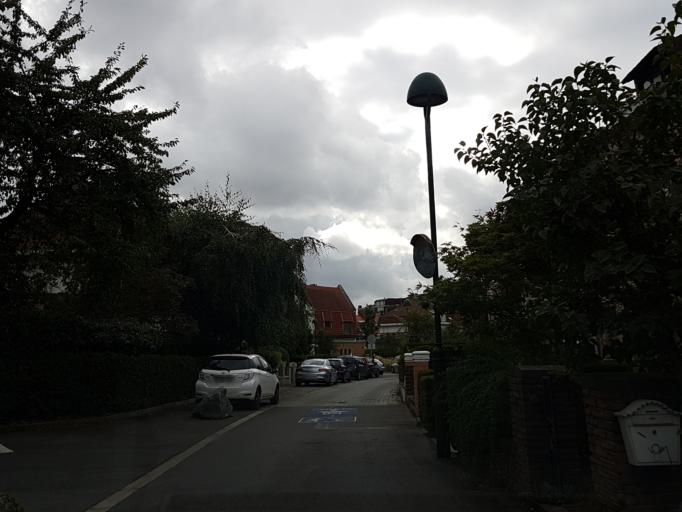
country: BE
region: Flanders
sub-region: Provincie Vlaams-Brabant
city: Diegem
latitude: 50.8662
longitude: 4.3958
